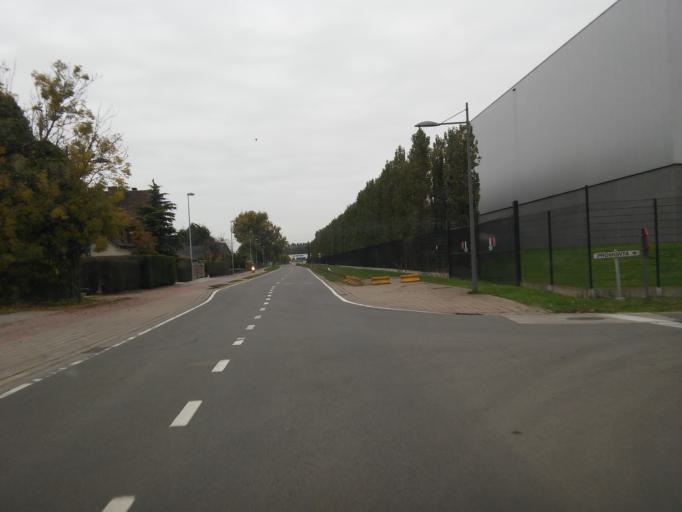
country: BE
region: Flanders
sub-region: Provincie Antwerpen
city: Willebroek
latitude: 51.0712
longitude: 4.3608
